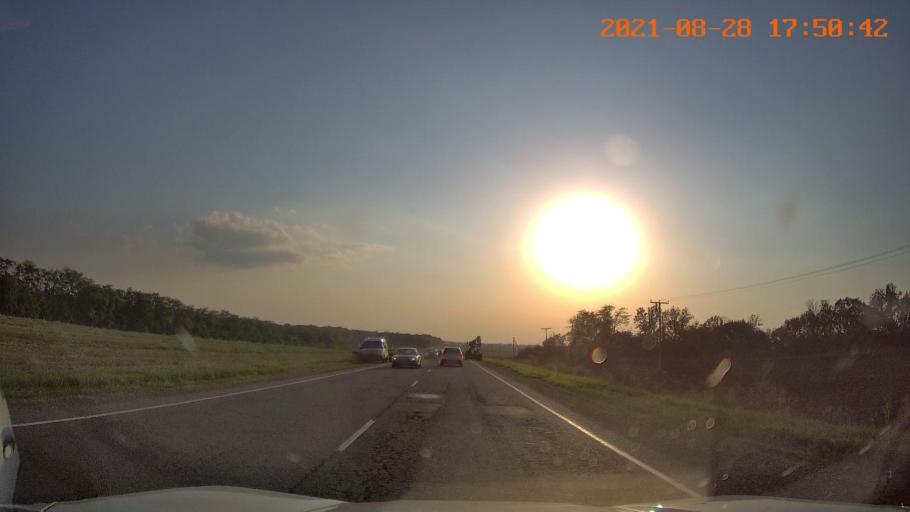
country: RU
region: Krasnodarskiy
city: Konstantinovskaya
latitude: 44.9462
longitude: 40.8086
